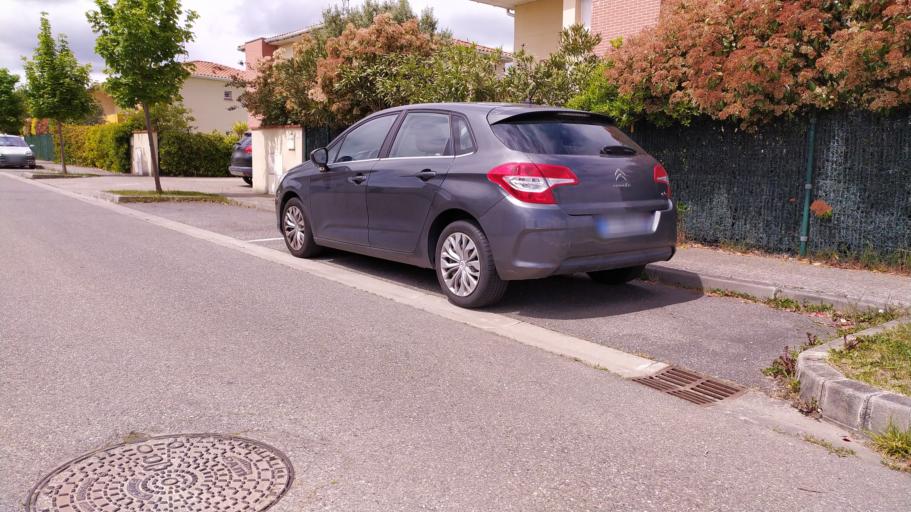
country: FR
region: Midi-Pyrenees
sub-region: Departement de la Haute-Garonne
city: La Salvetat-Saint-Gilles
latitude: 43.5822
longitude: 1.2893
